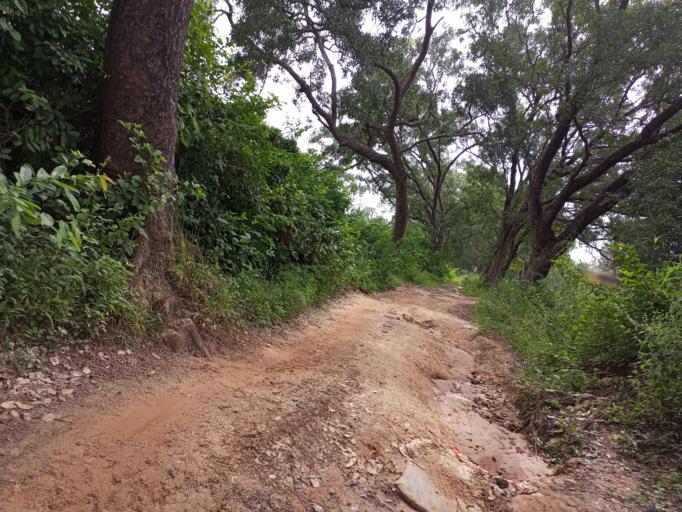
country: GW
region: Oio
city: Bissora
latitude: 12.4551
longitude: -15.4569
